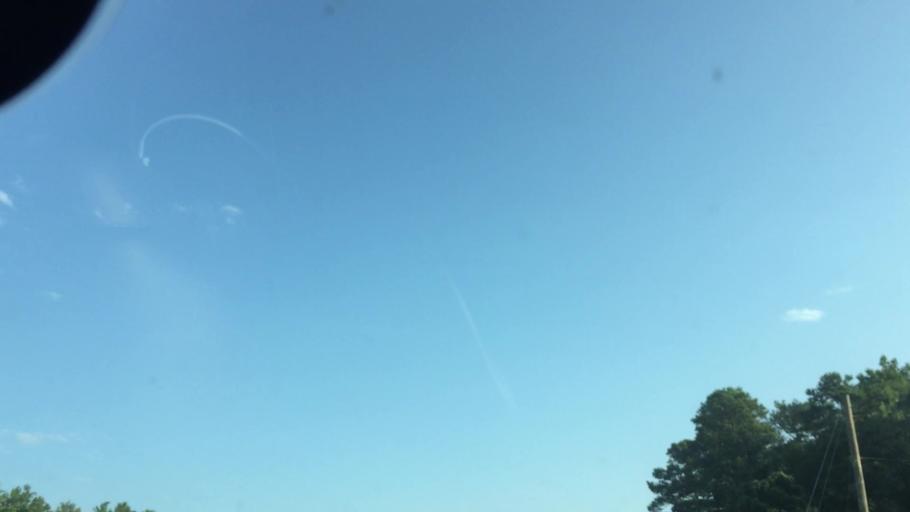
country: US
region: Georgia
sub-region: DeKalb County
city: Panthersville
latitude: 33.6871
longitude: -84.2023
